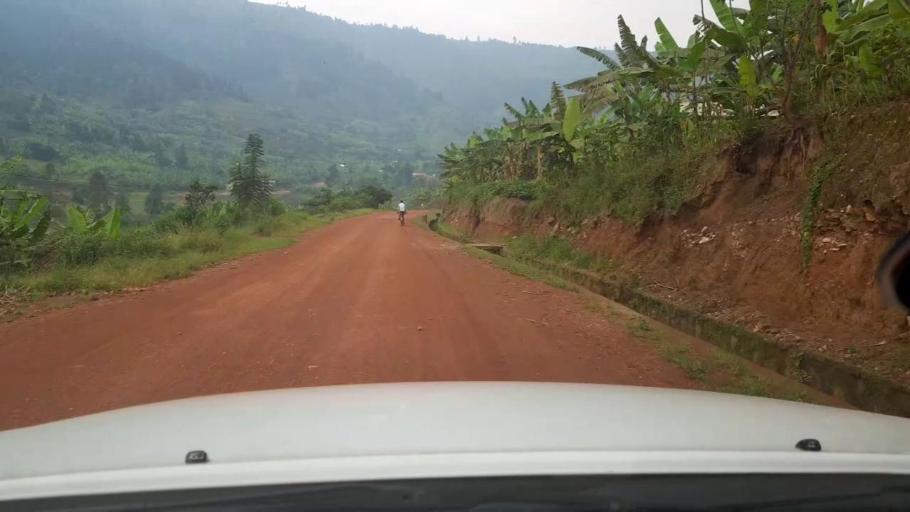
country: RW
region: Kigali
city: Kigali
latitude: -1.8548
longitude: 29.9046
